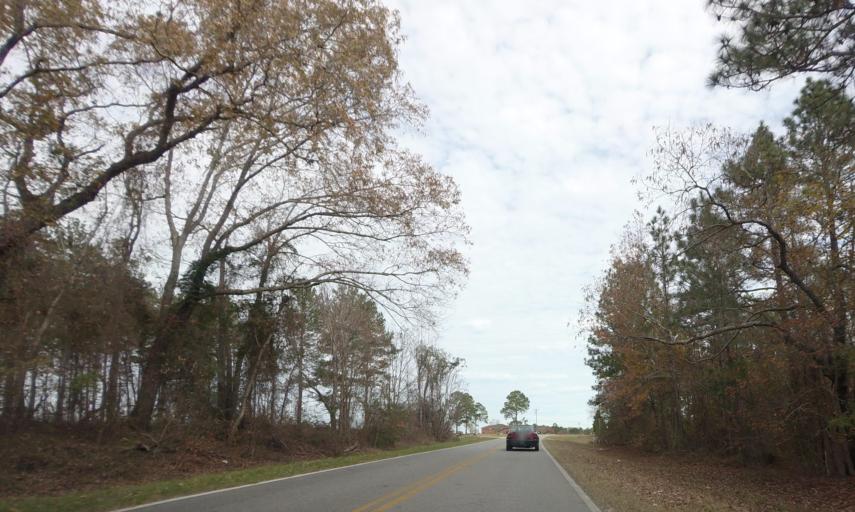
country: US
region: Georgia
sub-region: Dodge County
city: Chester
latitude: 32.4279
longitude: -83.1805
